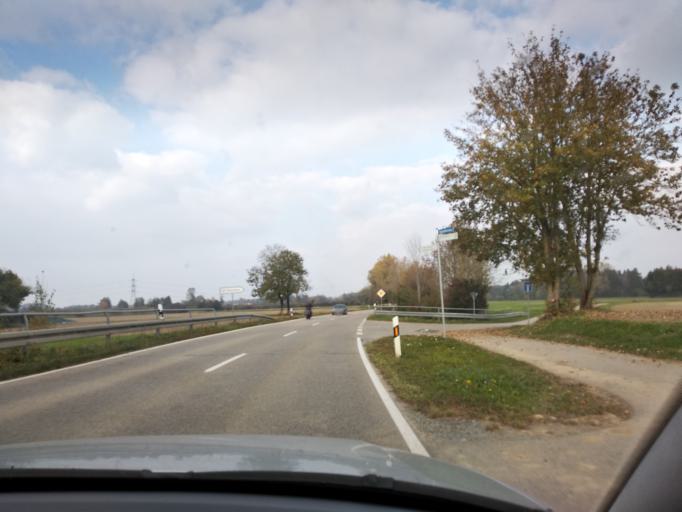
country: DE
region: Bavaria
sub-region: Upper Bavaria
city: Markt Schwaben
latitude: 48.1987
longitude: 11.8760
